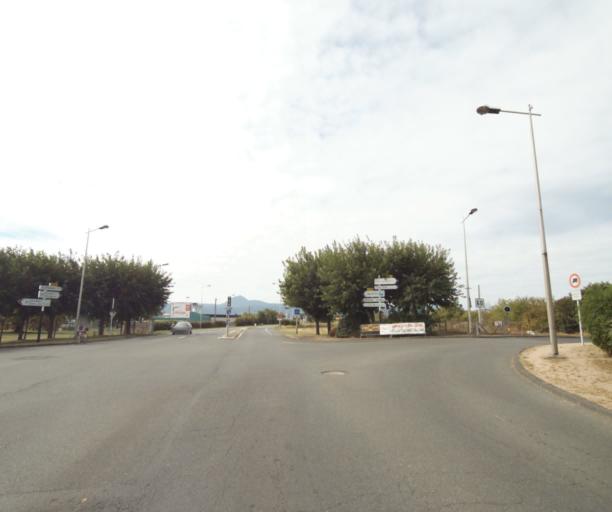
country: FR
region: Auvergne
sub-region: Departement du Puy-de-Dome
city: Aulnat
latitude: 45.7902
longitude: 3.1668
